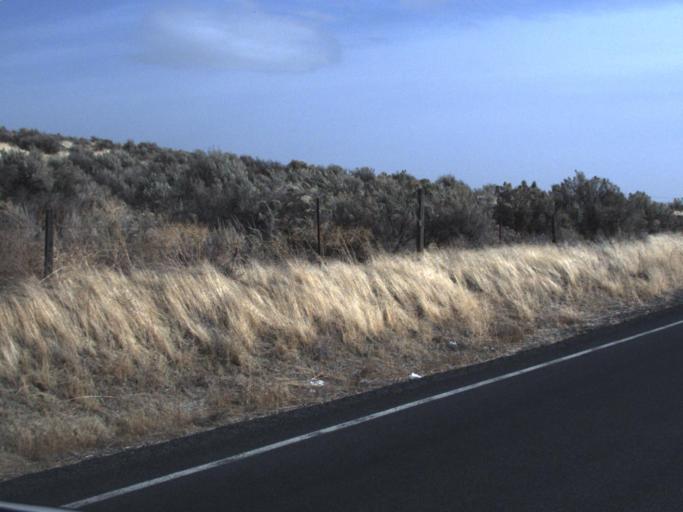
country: US
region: Washington
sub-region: Adams County
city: Ritzville
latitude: 47.3445
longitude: -118.6924
